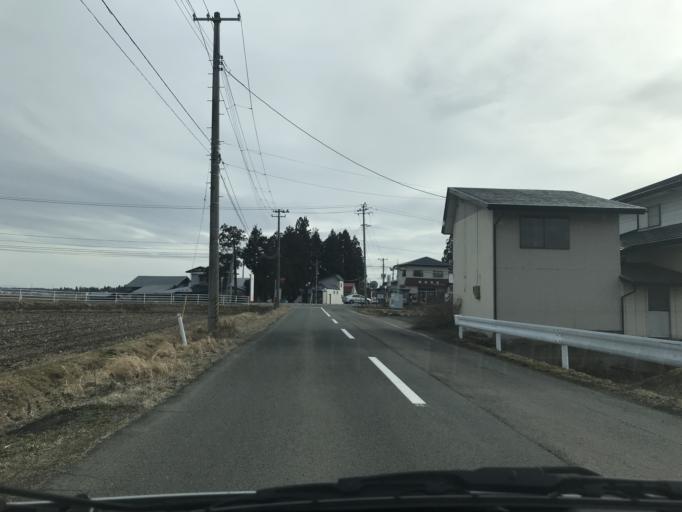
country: JP
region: Iwate
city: Hanamaki
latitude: 39.3666
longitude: 141.0685
